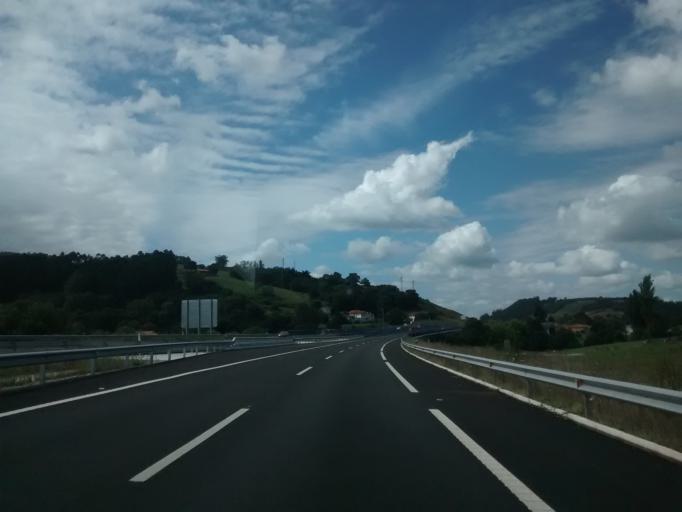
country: ES
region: Cantabria
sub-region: Provincia de Cantabria
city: Lierganes
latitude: 43.3583
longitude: -3.7641
